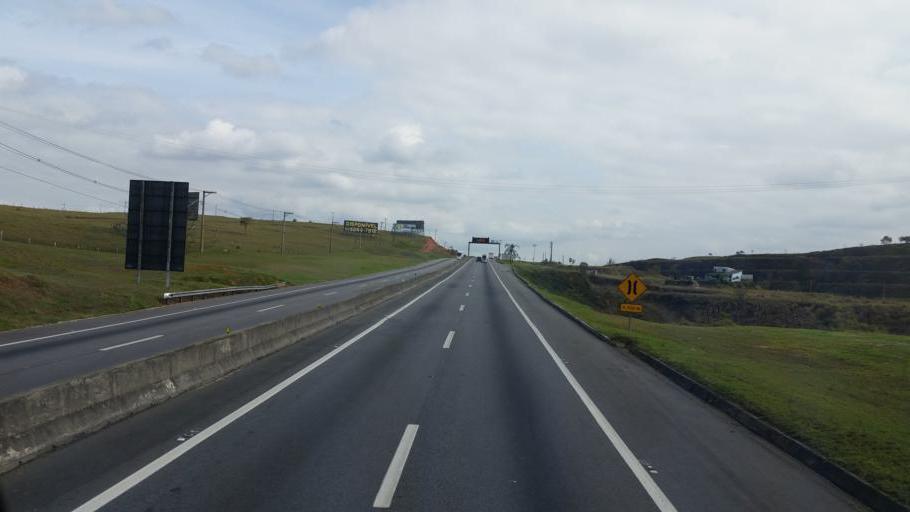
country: BR
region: Sao Paulo
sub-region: Guararema
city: Guararema
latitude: -23.3180
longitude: -46.0842
